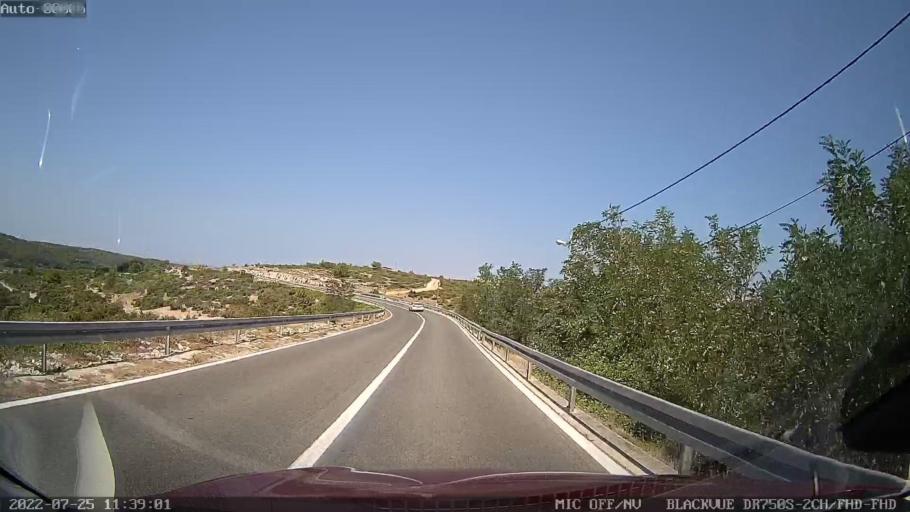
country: HR
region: Zadarska
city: Razanac
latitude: 44.2557
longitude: 15.3760
